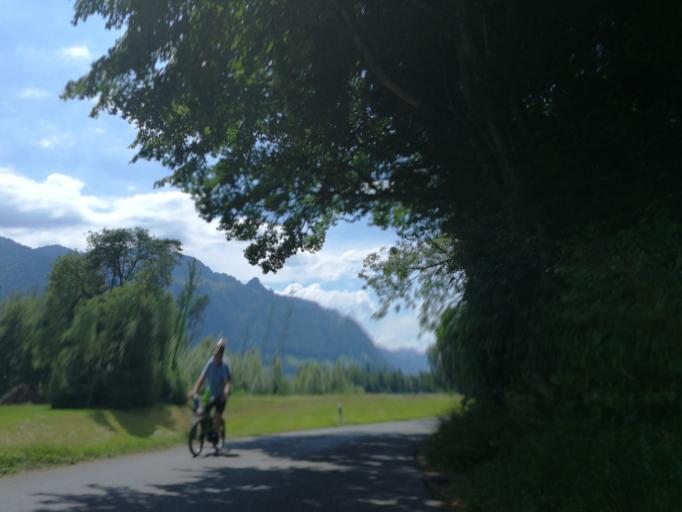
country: CH
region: Glarus
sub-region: Glarus
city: Bilten
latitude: 47.1731
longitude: 9.0148
